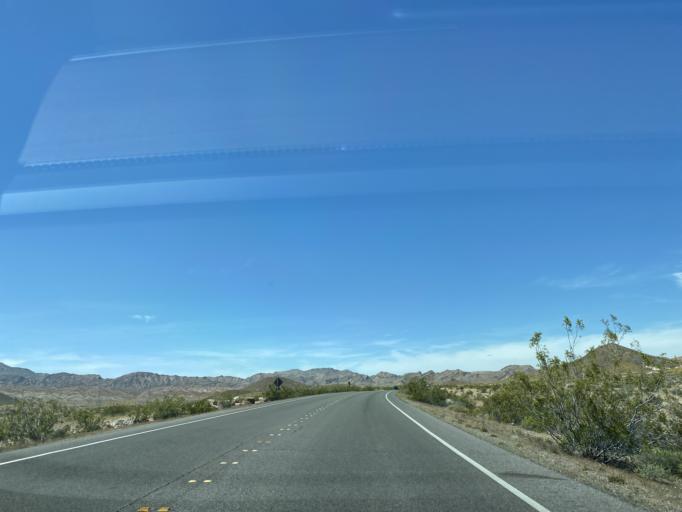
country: US
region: Nevada
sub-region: Clark County
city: Henderson
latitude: 36.1636
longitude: -114.9082
